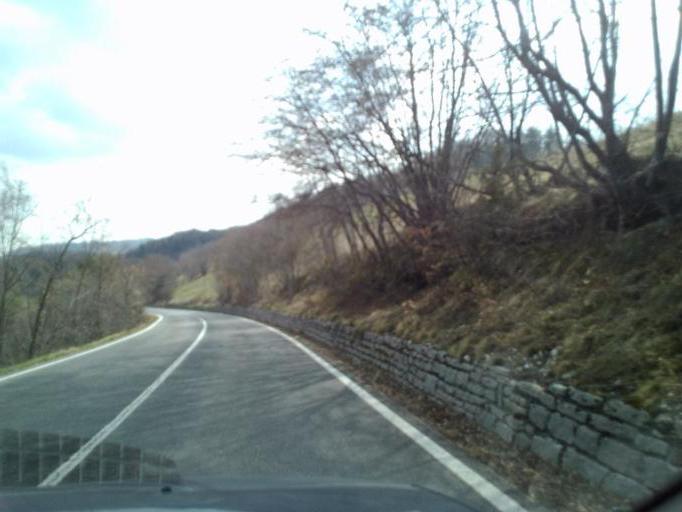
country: IT
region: Veneto
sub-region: Provincia di Verona
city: Sant'Anna d'Alfaedo
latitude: 45.6158
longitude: 10.9477
